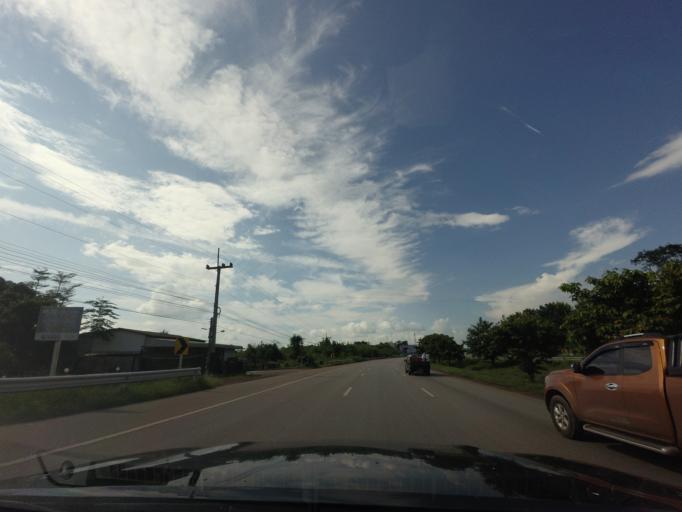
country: TH
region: Nong Khai
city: Sa Khrai
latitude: 17.6802
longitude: 102.7851
